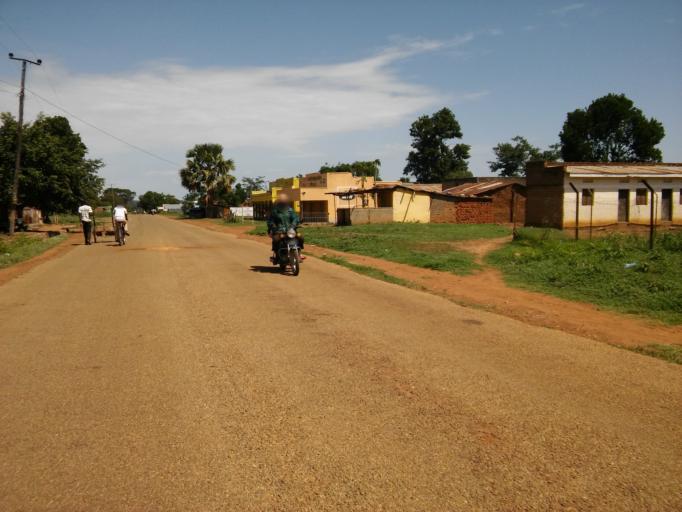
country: UG
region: Eastern Region
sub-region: Kumi District
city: Kumi
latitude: 1.4866
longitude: 33.9274
